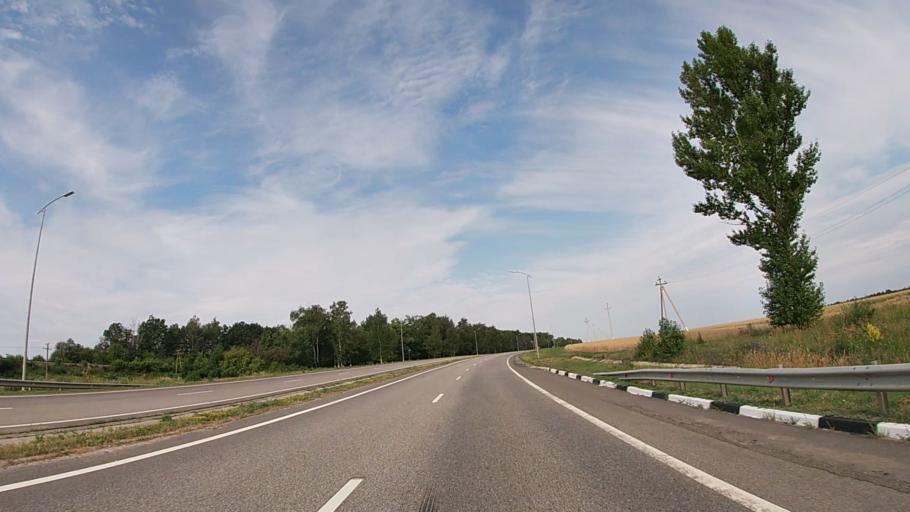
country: RU
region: Belgorod
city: Borisovka
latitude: 50.7496
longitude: 35.9914
